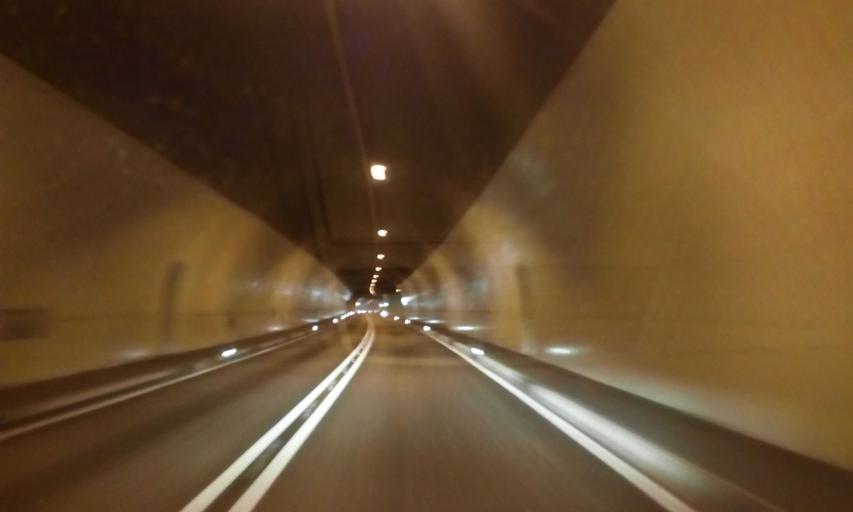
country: CH
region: Grisons
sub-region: Hinterrhein District
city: Thusis
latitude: 46.6970
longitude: 9.4582
